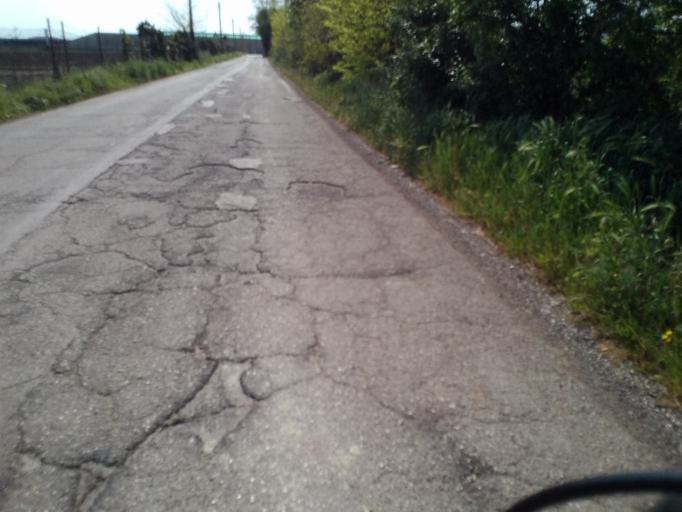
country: IT
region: Veneto
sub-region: Provincia di Verona
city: Dossobuono
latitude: 45.4033
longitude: 10.9428
